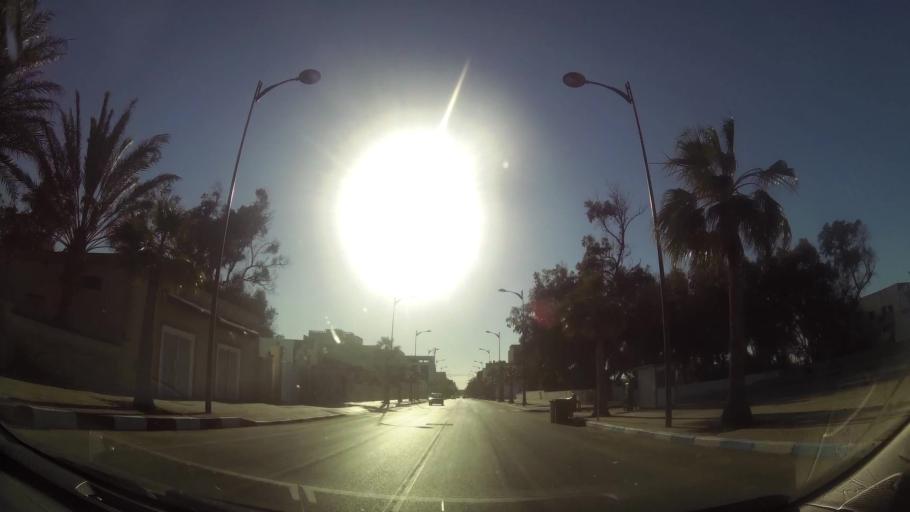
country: MA
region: Oriental
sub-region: Berkane-Taourirt
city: Madagh
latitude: 35.0843
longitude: -2.2187
